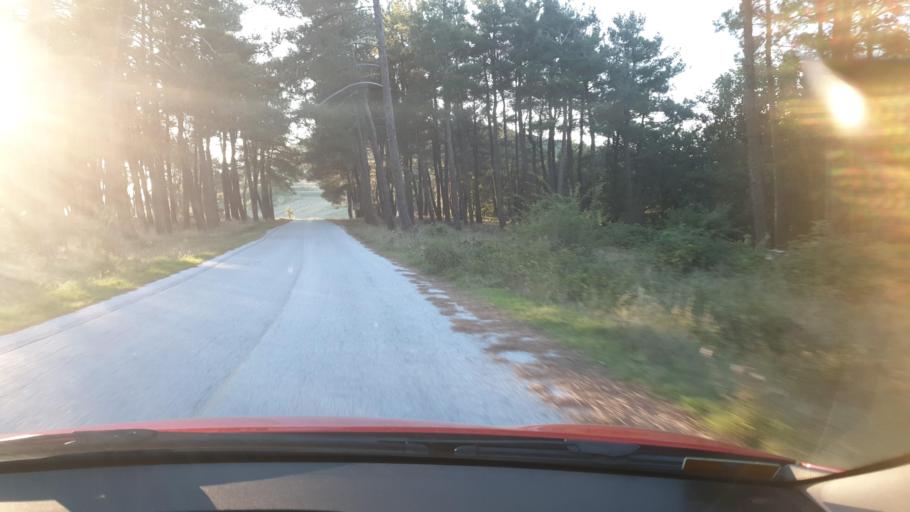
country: GR
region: Central Macedonia
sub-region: Nomos Thessalonikis
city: Peristera
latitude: 40.5126
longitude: 23.2164
